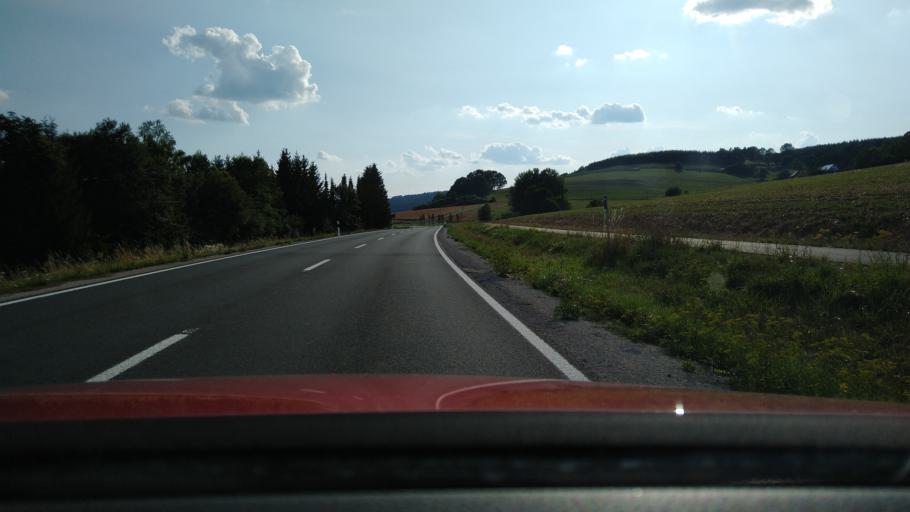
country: DE
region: Bavaria
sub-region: Upper Franconia
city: Glashutten
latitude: 49.9201
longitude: 11.4023
